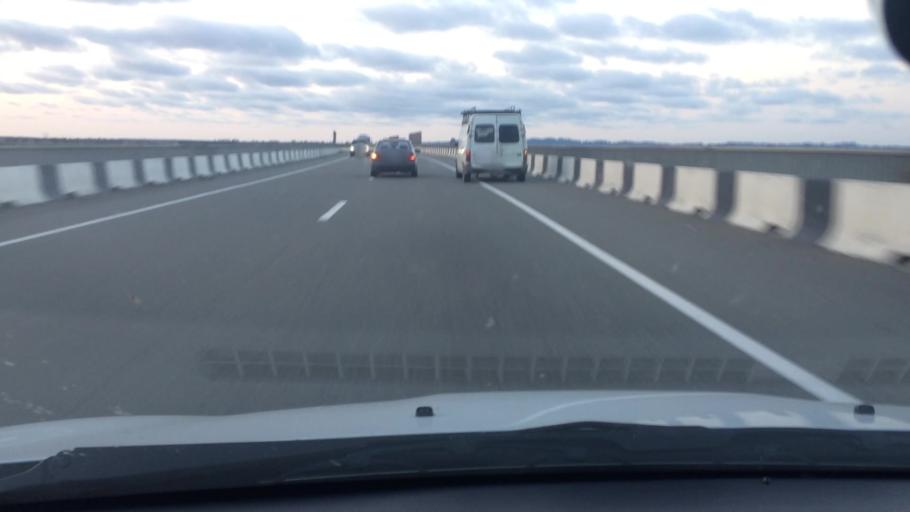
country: GE
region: Ajaria
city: Ochkhamuri
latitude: 41.8652
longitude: 41.8365
